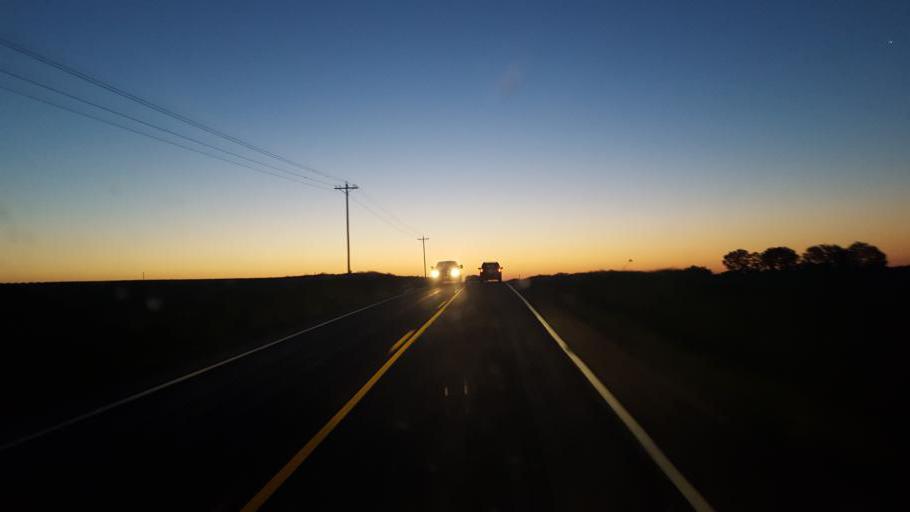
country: US
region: Missouri
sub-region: Mercer County
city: Princeton
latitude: 40.4147
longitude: -93.5011
